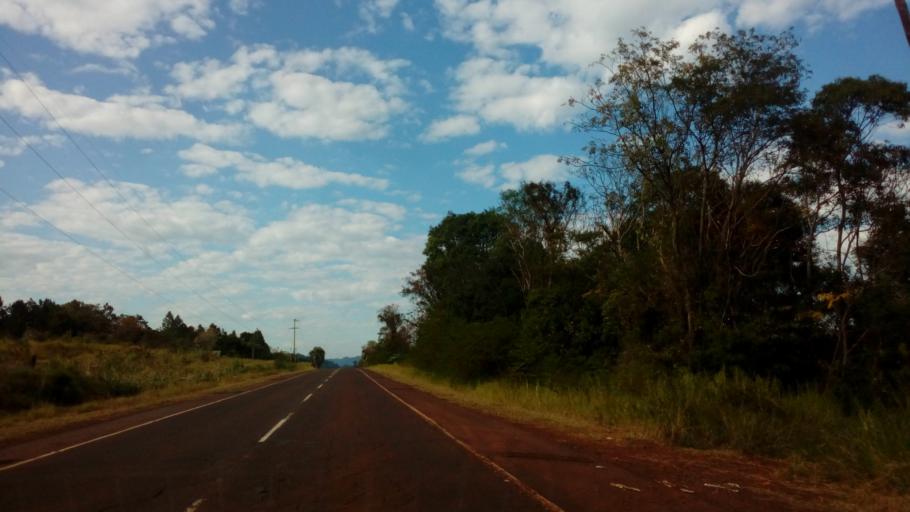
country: AR
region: Misiones
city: Ruiz de Montoya
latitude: -27.0655
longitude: -54.9941
